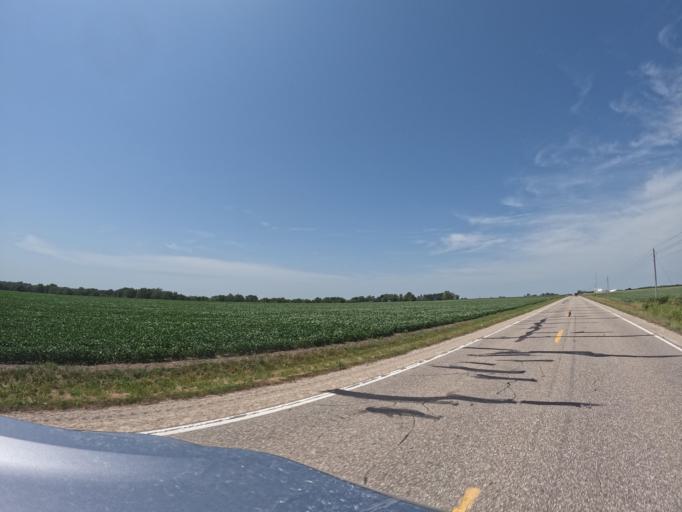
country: US
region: Iowa
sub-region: Henry County
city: Mount Pleasant
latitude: 40.9921
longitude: -91.6122
